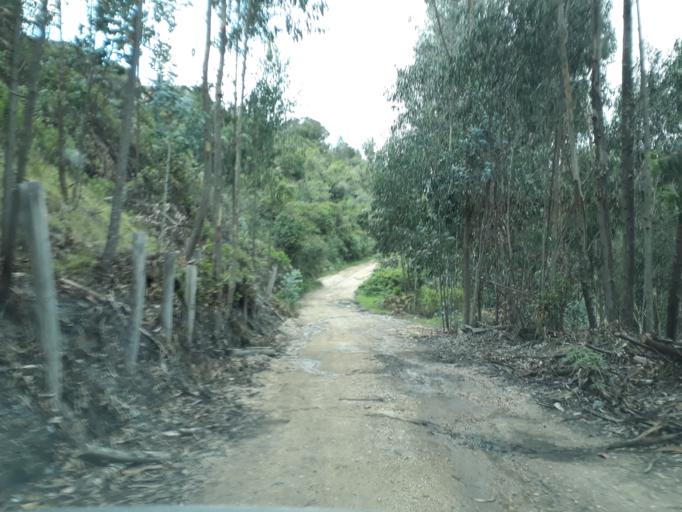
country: CO
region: Cundinamarca
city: Lenguazaque
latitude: 5.2706
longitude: -73.6890
